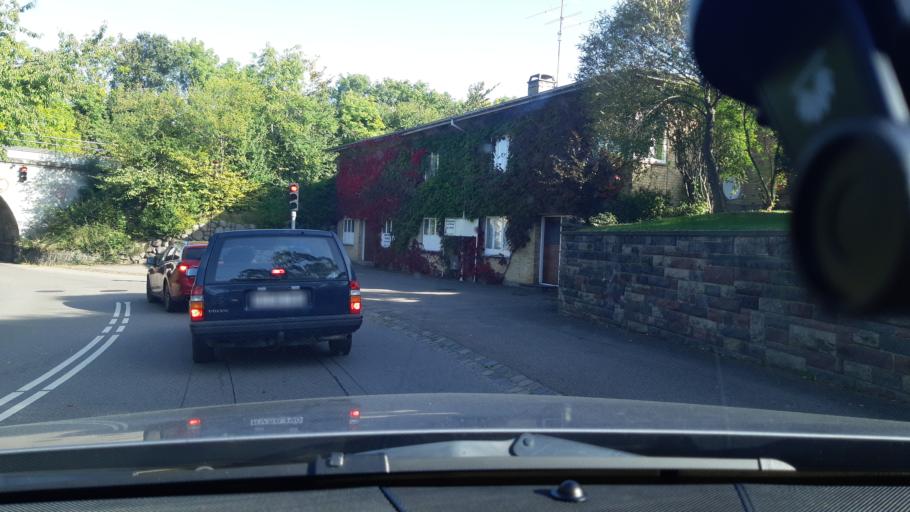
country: DK
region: Zealand
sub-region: Holbaek Kommune
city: Holbaek
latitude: 55.7150
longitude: 11.6882
